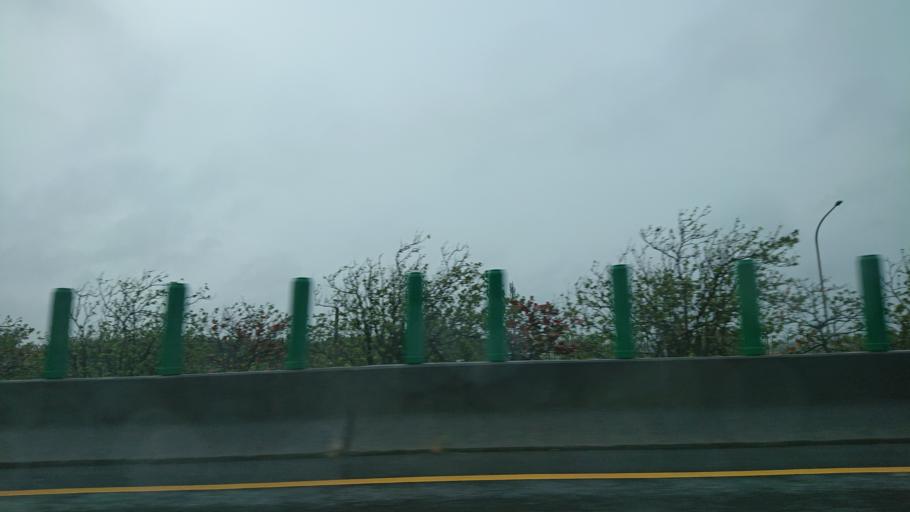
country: TW
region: Taiwan
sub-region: Chiayi
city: Taibao
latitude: 23.7245
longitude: 120.2180
